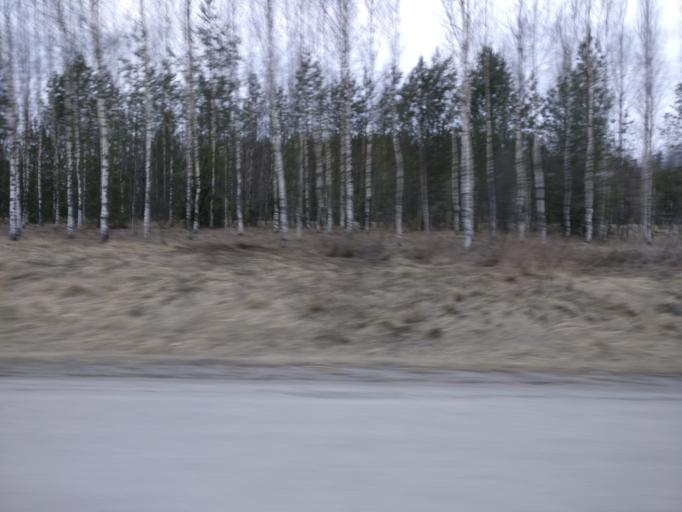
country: FI
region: Uusimaa
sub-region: Helsinki
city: Nurmijaervi
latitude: 60.4081
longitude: 24.8225
